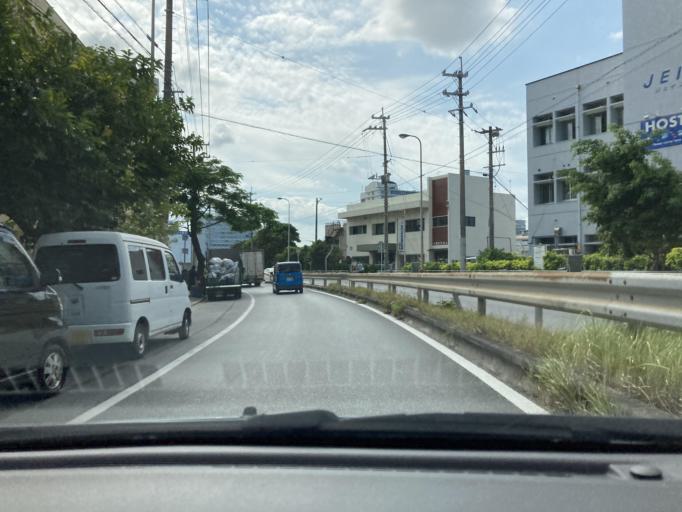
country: JP
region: Okinawa
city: Naha-shi
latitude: 26.2271
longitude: 127.6817
